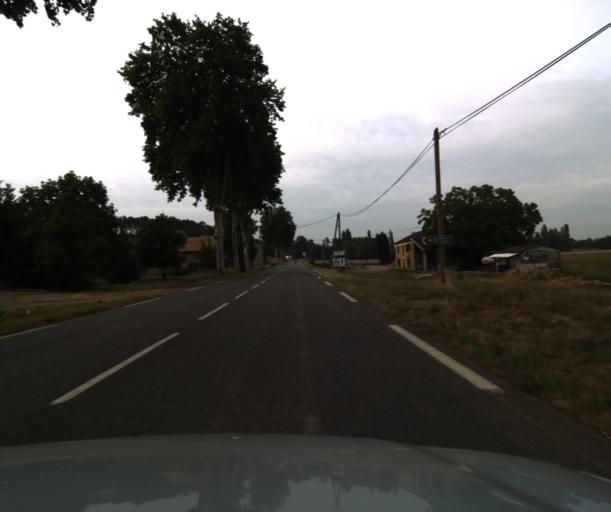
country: FR
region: Midi-Pyrenees
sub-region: Departement du Gers
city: Mirande
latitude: 43.5268
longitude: 0.4165
